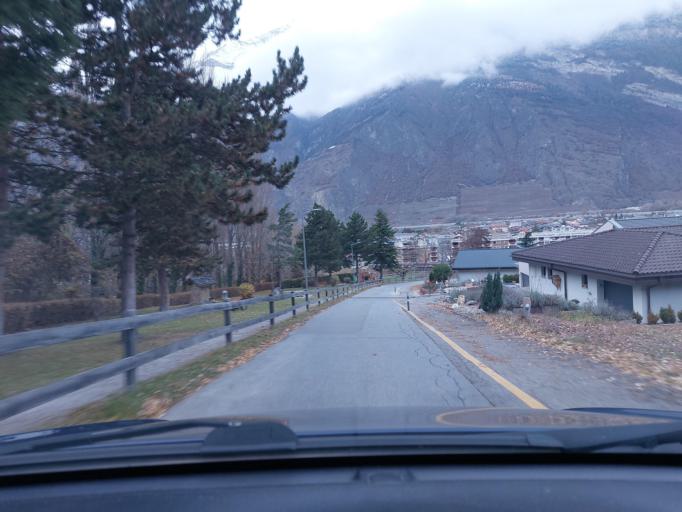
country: CH
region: Valais
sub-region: Martigny District
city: Saxon
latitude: 46.1463
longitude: 7.1767
